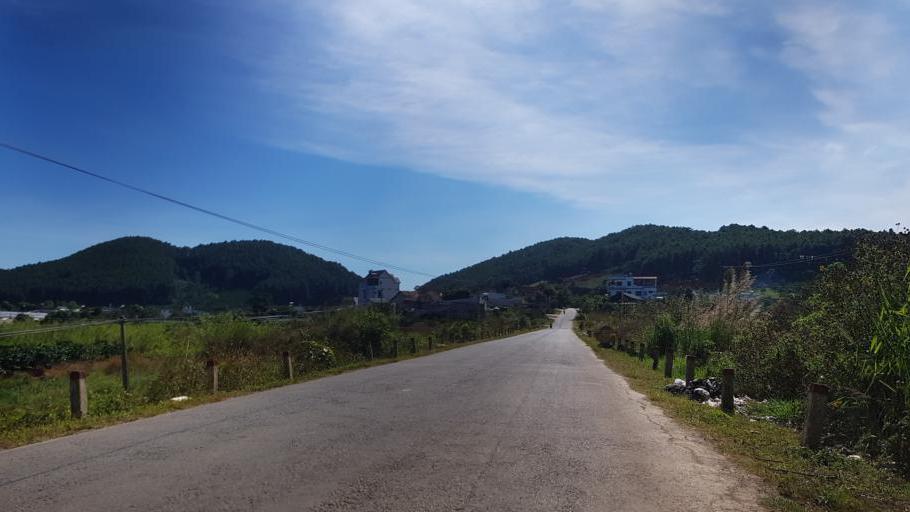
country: VN
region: Lam Dong
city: Da Lat
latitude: 11.8766
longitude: 108.3424
